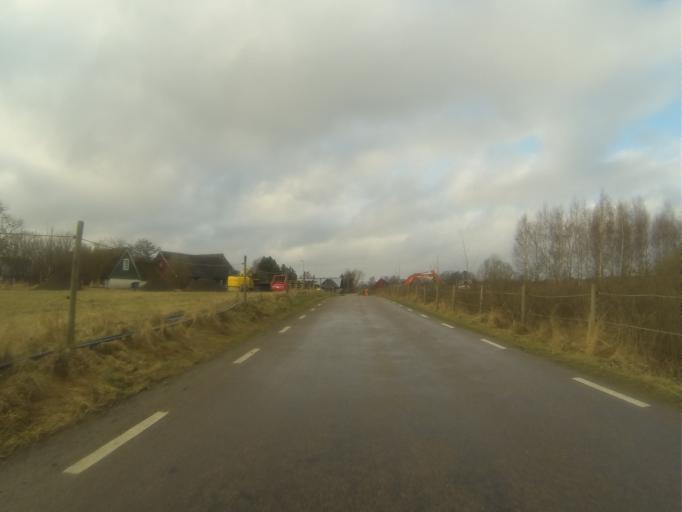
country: SE
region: Skane
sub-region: Svedala Kommun
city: Klagerup
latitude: 55.5692
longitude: 13.3073
